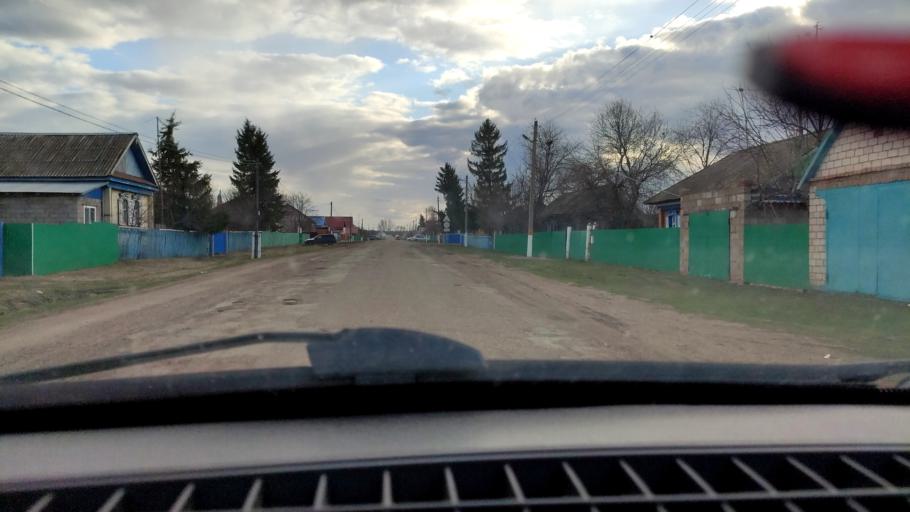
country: RU
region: Bashkortostan
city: Karmaskaly
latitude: 54.3356
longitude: 55.9983
